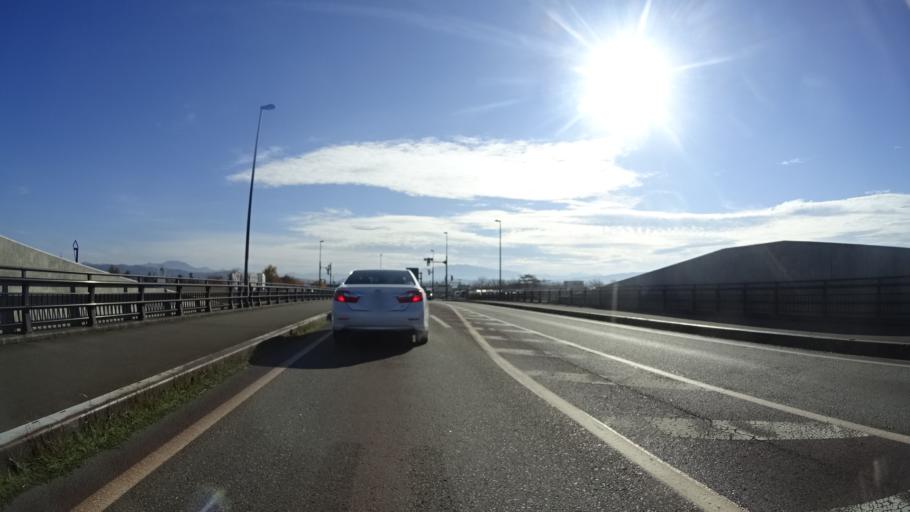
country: JP
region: Niigata
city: Mitsuke
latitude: 37.5455
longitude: 138.8821
